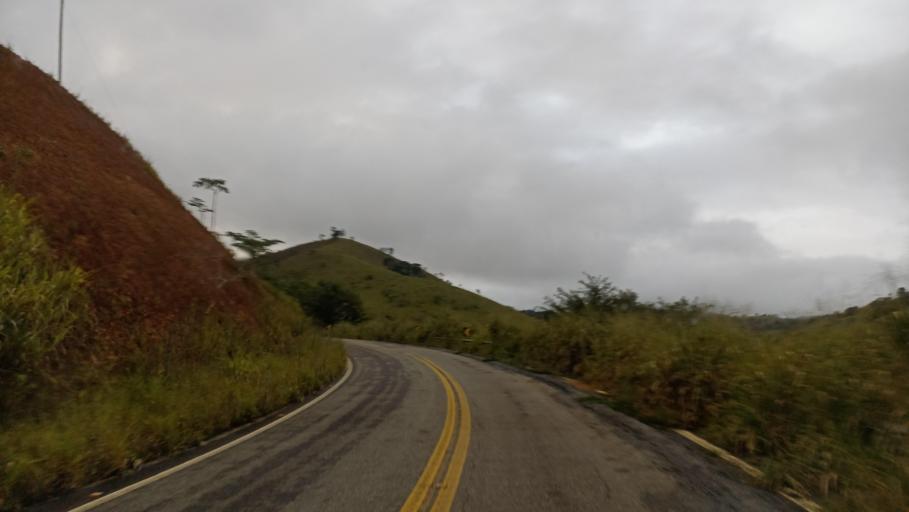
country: BR
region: Minas Gerais
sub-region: Joaima
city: Joaima
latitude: -16.6896
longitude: -40.5214
